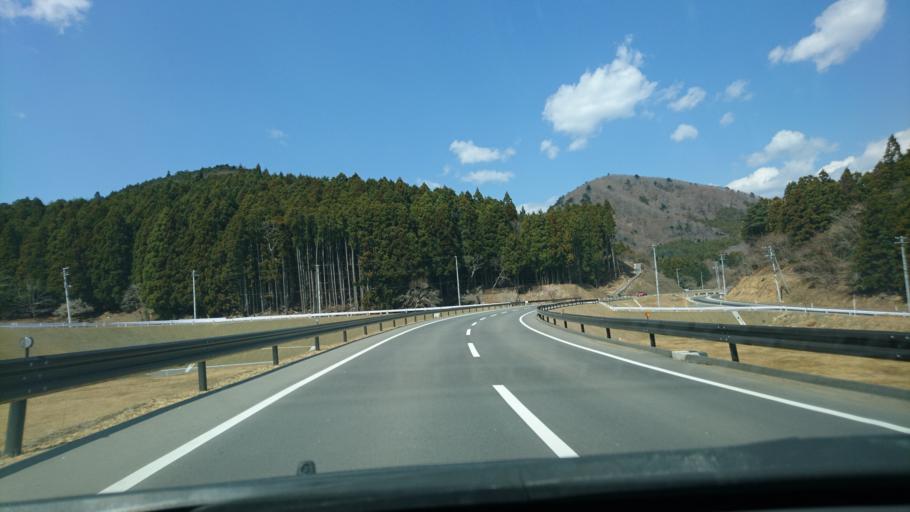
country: JP
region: Miyagi
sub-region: Oshika Gun
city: Onagawa Cho
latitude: 38.4638
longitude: 141.4734
